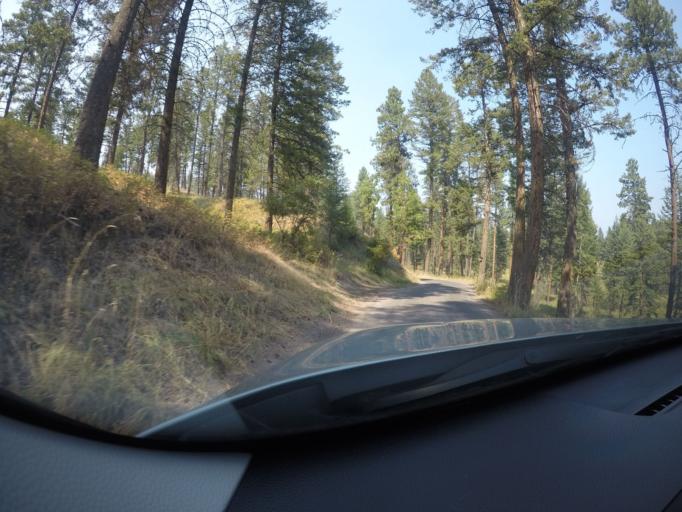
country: US
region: Montana
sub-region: Lake County
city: Polson
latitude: 47.7703
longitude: -114.1425
